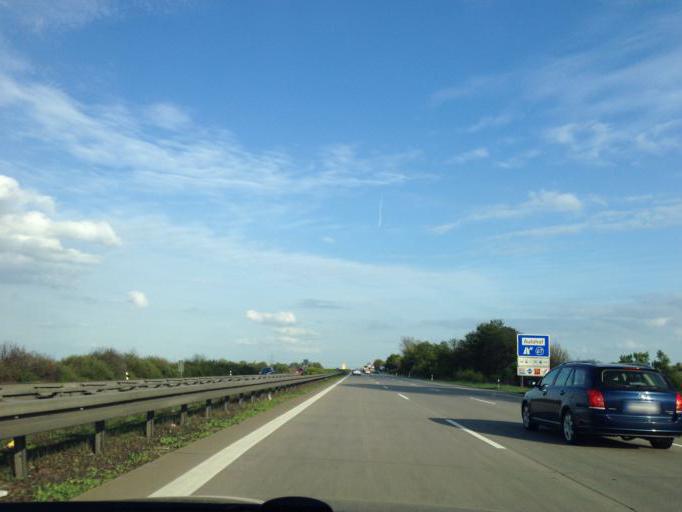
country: DE
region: Saxony-Anhalt
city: Gross Santersleben
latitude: 52.1817
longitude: 11.4613
